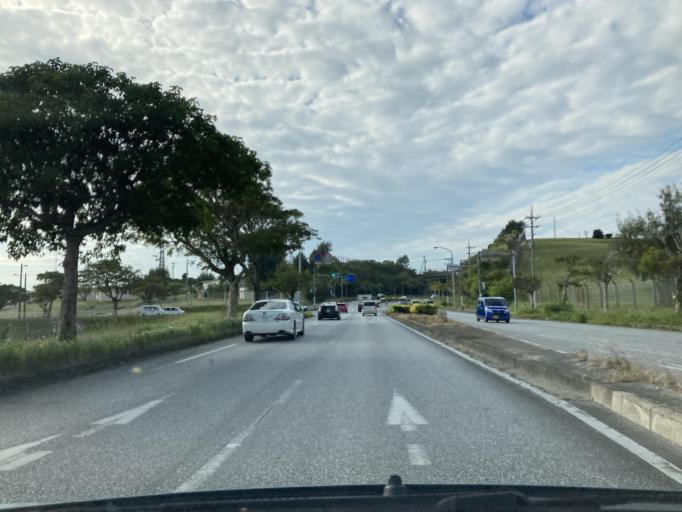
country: JP
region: Okinawa
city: Okinawa
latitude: 26.3166
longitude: 127.7929
